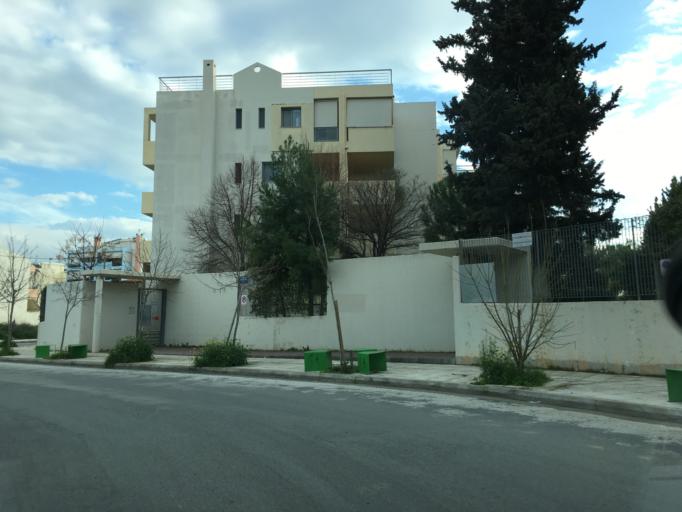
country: GR
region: Attica
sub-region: Nomarchia Athinas
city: Marousi
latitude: 38.0416
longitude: 23.7939
